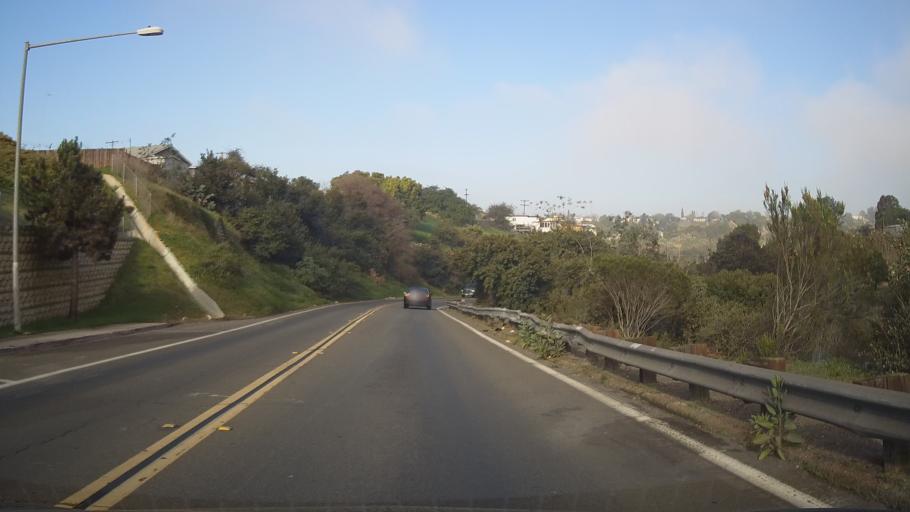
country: US
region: California
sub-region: San Diego County
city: National City
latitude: 32.7274
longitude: -117.0862
